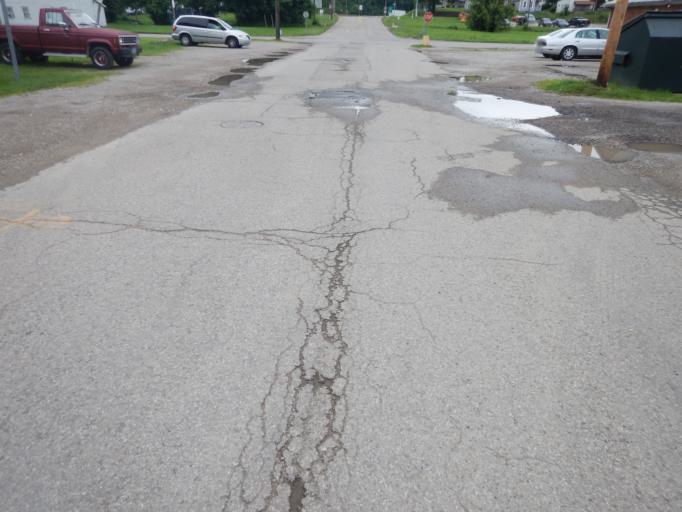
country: US
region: Ohio
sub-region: Muskingum County
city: Zanesville
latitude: 39.9459
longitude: -82.0216
